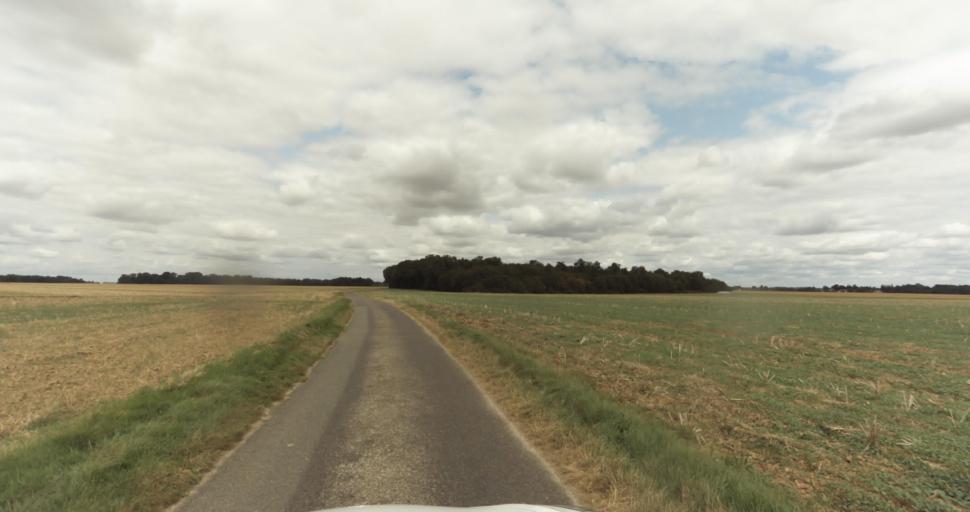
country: FR
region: Haute-Normandie
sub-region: Departement de l'Eure
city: Saint-Germain-sur-Avre
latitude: 48.8051
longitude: 1.2654
